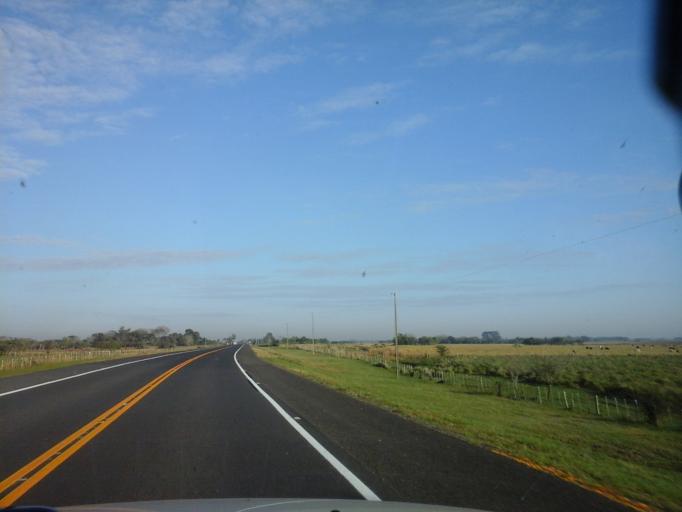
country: PY
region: Neembucu
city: Cerrito
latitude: -26.8665
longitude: -57.5758
